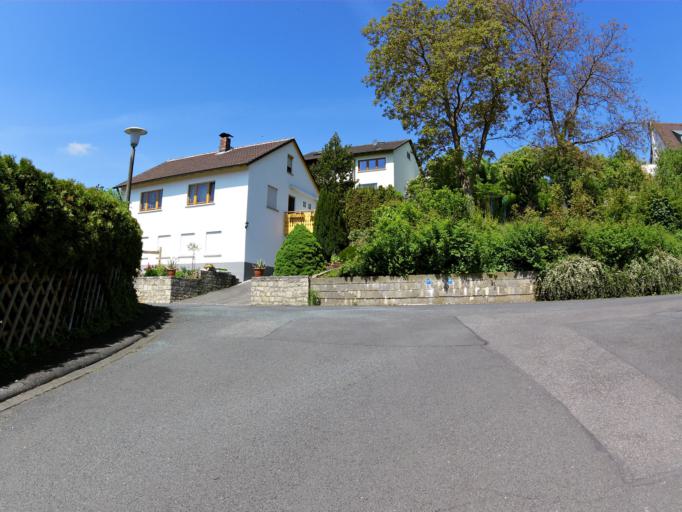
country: DE
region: Bavaria
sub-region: Regierungsbezirk Unterfranken
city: Theilheim
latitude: 49.7349
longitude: 10.0321
